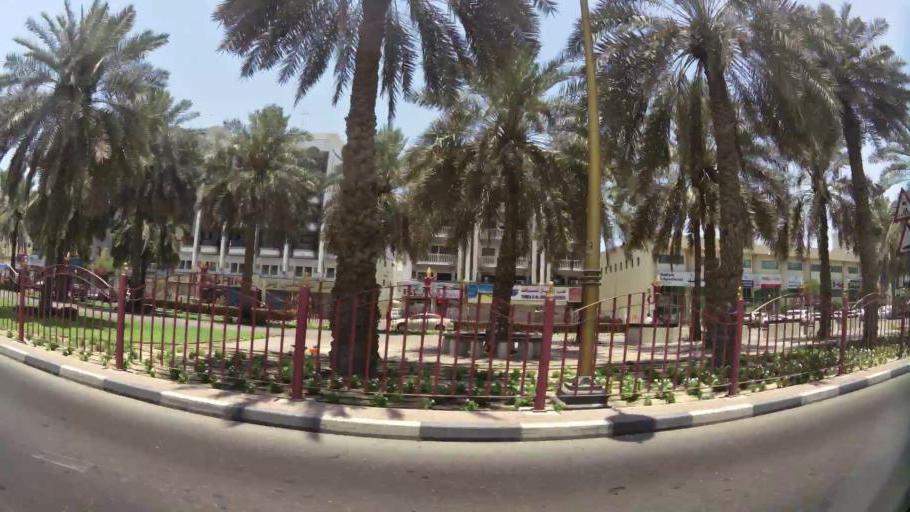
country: AE
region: Ash Shariqah
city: Sharjah
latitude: 25.2740
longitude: 55.3247
